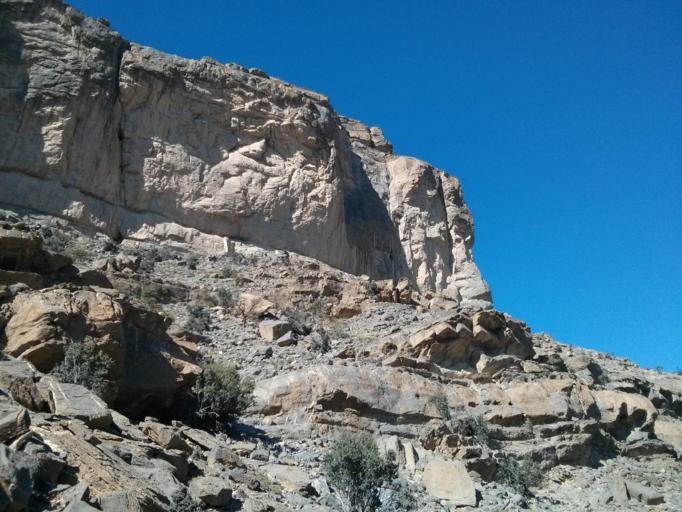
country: OM
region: Muhafazat ad Dakhiliyah
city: Bahla'
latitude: 23.2069
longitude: 57.2056
